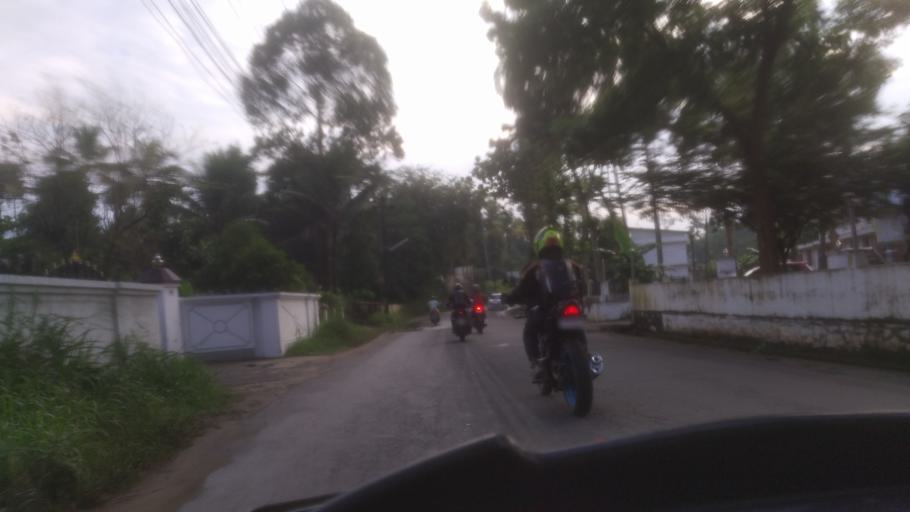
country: IN
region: Kerala
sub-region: Ernakulam
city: Perumpavur
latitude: 10.1112
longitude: 76.5291
